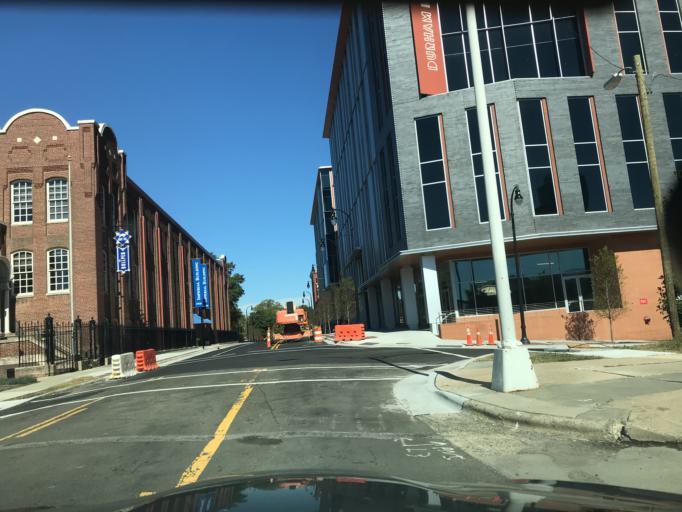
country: US
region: North Carolina
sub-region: Durham County
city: Durham
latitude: 35.9986
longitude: -78.9037
